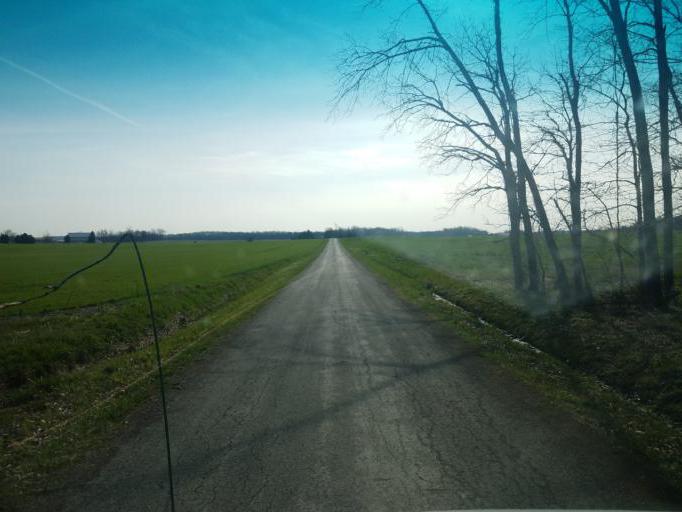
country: US
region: Ohio
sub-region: Richland County
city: Shelby
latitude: 40.8871
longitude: -82.5605
